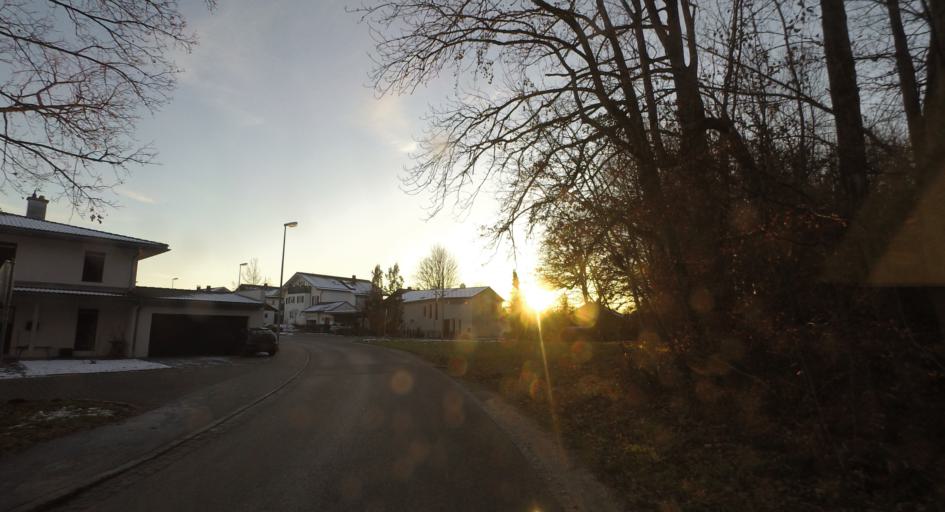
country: DE
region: Bavaria
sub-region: Upper Bavaria
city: Traunstein
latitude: 47.8823
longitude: 12.6264
